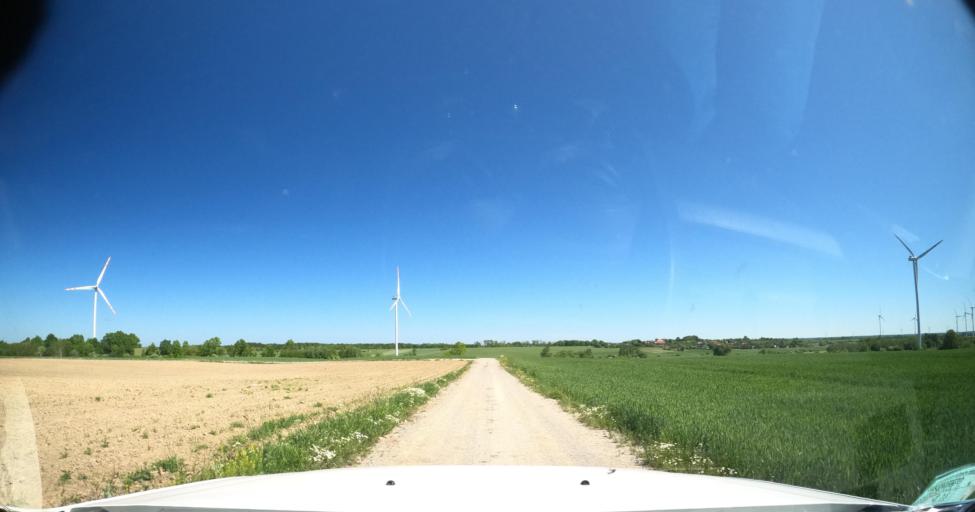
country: PL
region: Pomeranian Voivodeship
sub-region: Powiat slupski
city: Ustka
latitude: 54.5110
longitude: 16.7470
